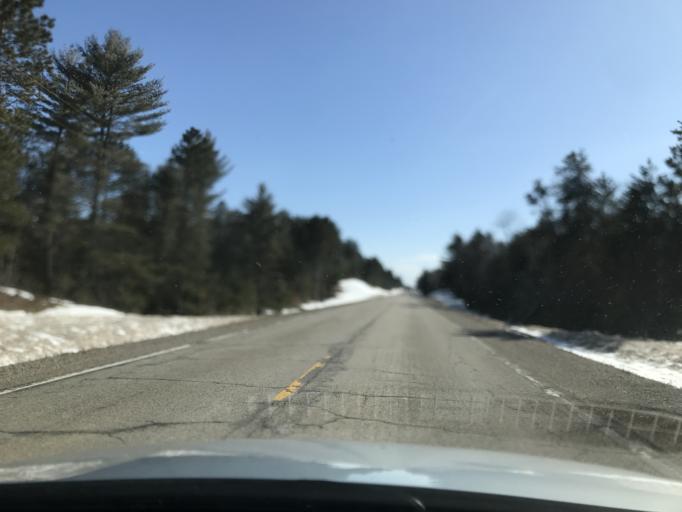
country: US
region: Wisconsin
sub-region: Marinette County
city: Niagara
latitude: 45.3937
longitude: -88.0995
